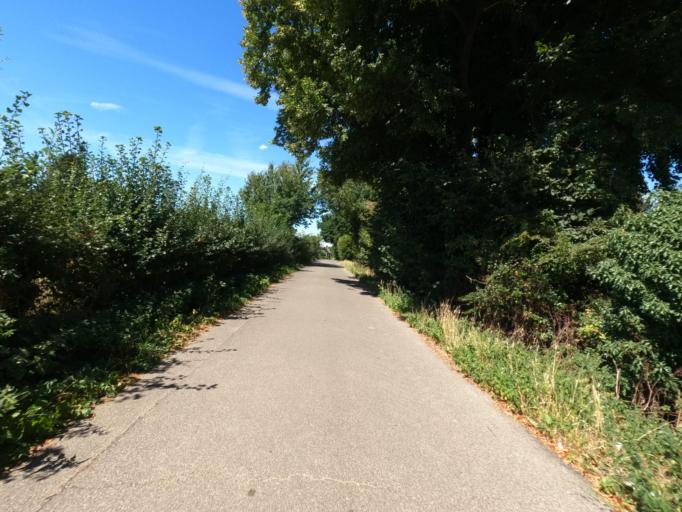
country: DE
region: North Rhine-Westphalia
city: Baesweiler
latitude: 50.8916
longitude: 6.1860
